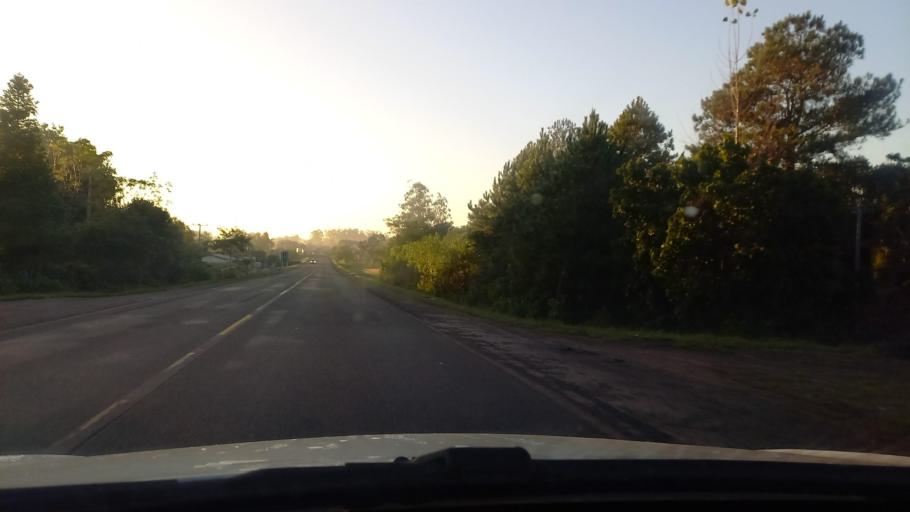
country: BR
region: Rio Grande do Sul
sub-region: Candelaria
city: Candelaria
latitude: -29.6815
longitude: -52.8191
